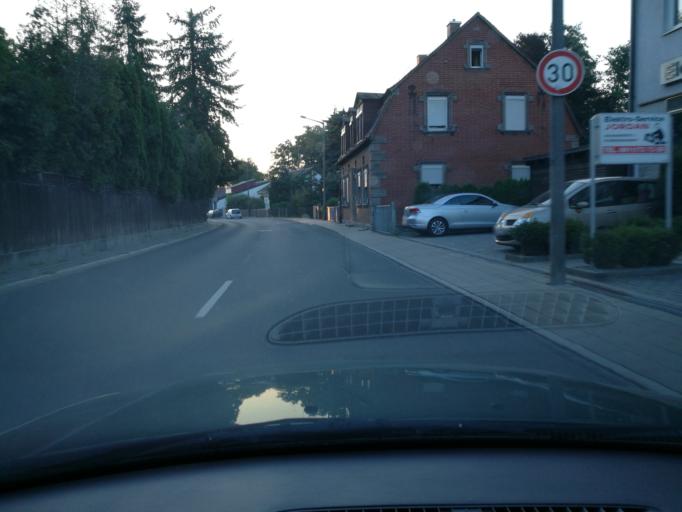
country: DE
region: Bavaria
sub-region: Regierungsbezirk Mittelfranken
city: Furth
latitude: 49.4920
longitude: 10.9568
